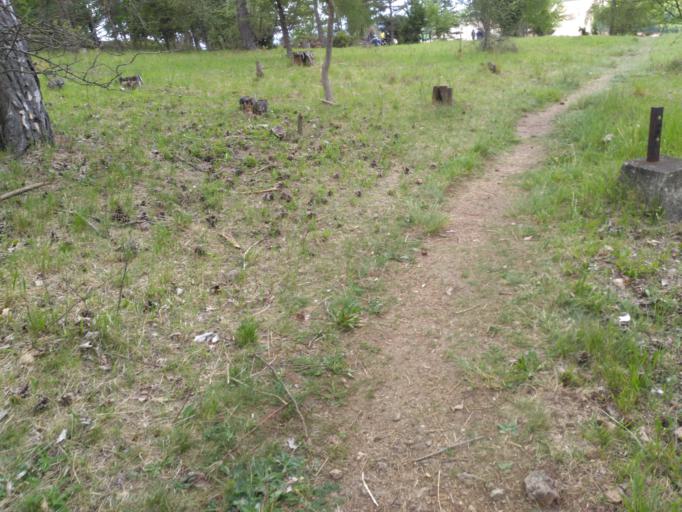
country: CZ
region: Central Bohemia
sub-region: Okres Beroun
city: Kraluv Dvur
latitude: 49.9158
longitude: 14.0651
